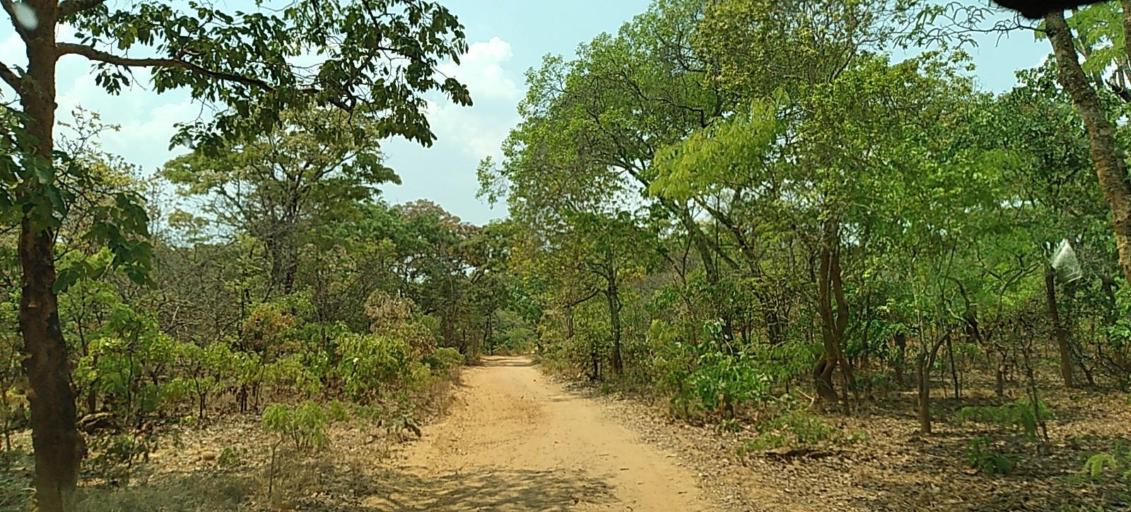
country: ZM
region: North-Western
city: Kabompo
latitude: -13.6478
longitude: 24.3764
